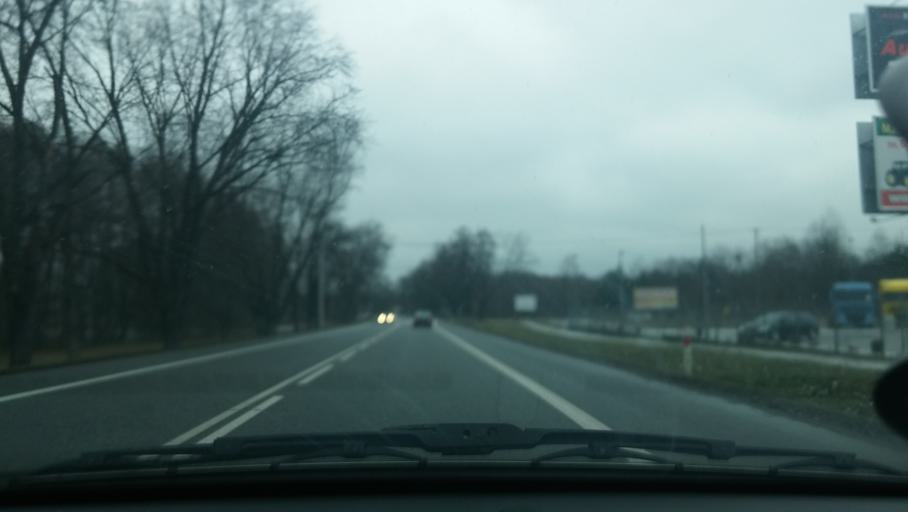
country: PL
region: Masovian Voivodeship
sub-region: Powiat minski
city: Kaluszyn
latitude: 52.2021
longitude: 21.7951
